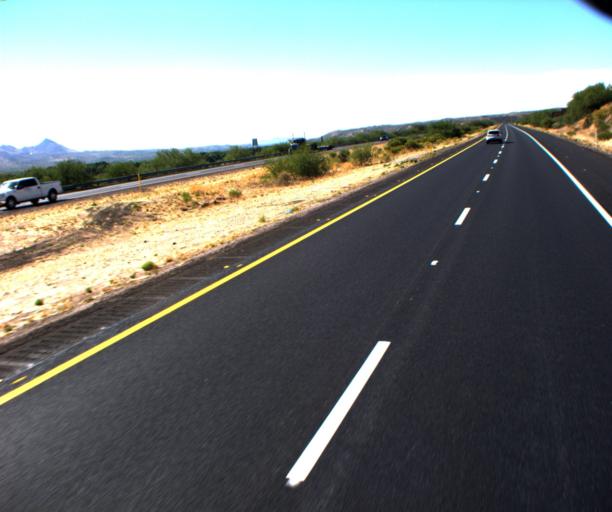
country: US
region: Arizona
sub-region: Santa Cruz County
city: Tubac
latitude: 31.5668
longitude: -111.0538
